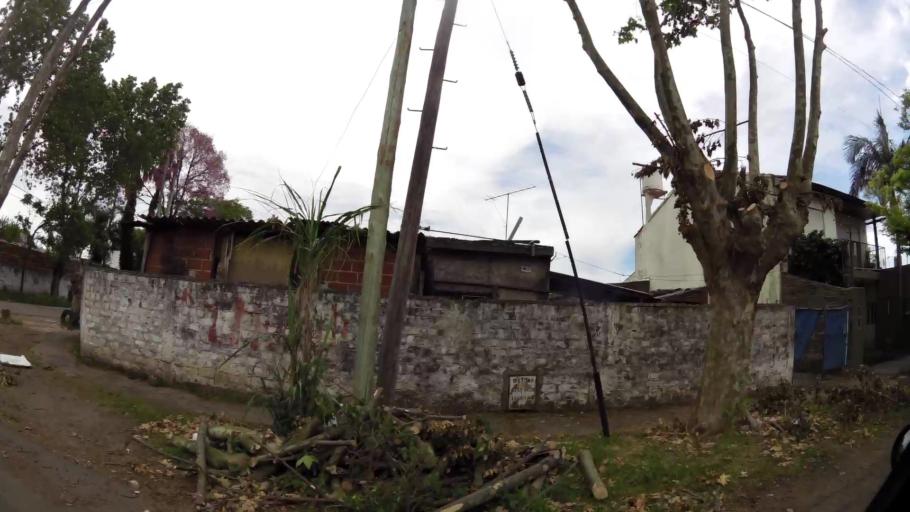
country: AR
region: Buenos Aires
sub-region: Partido de Quilmes
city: Quilmes
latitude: -34.7598
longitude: -58.2315
